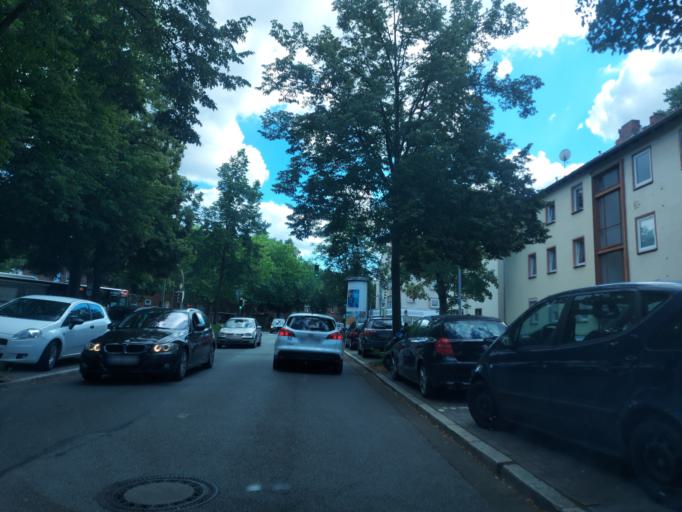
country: DE
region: Lower Saxony
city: Osnabrueck
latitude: 52.2606
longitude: 8.0452
